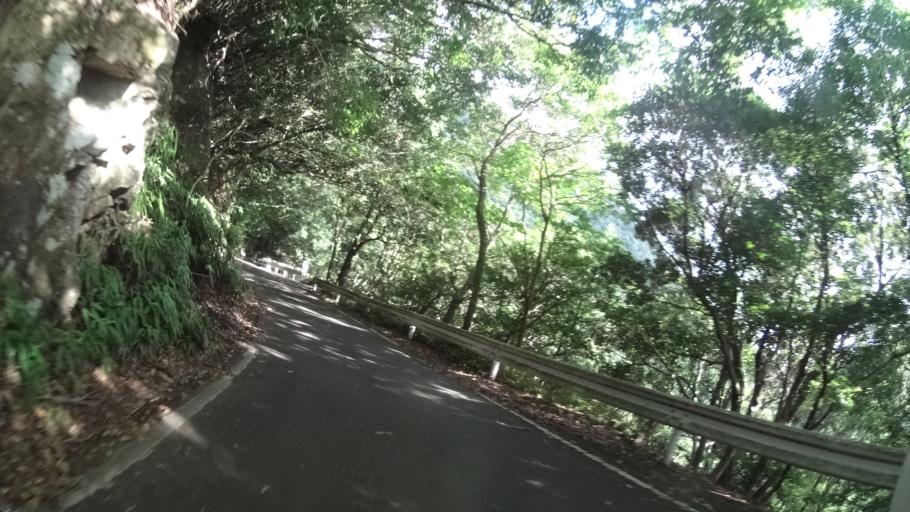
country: JP
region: Kagoshima
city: Nishinoomote
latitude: 30.3378
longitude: 130.3962
